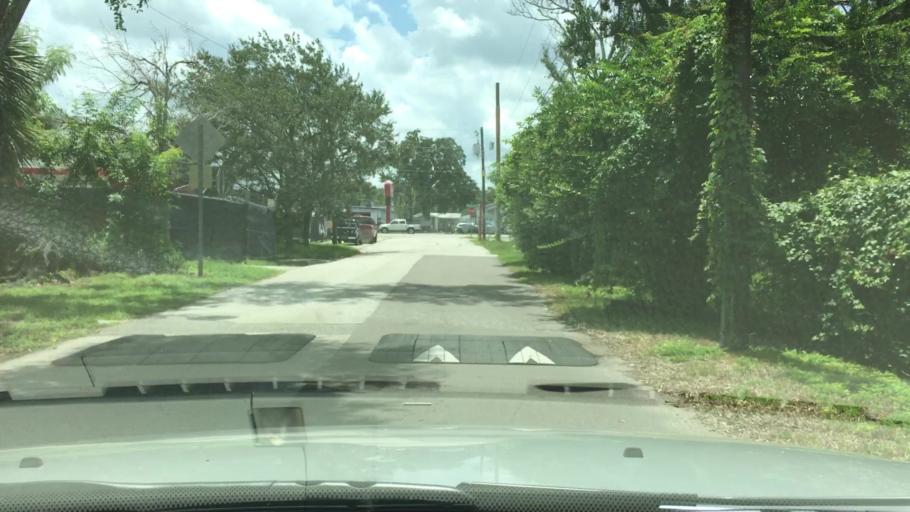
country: US
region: Florida
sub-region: Volusia County
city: Holly Hill
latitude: 29.2259
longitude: -81.0352
